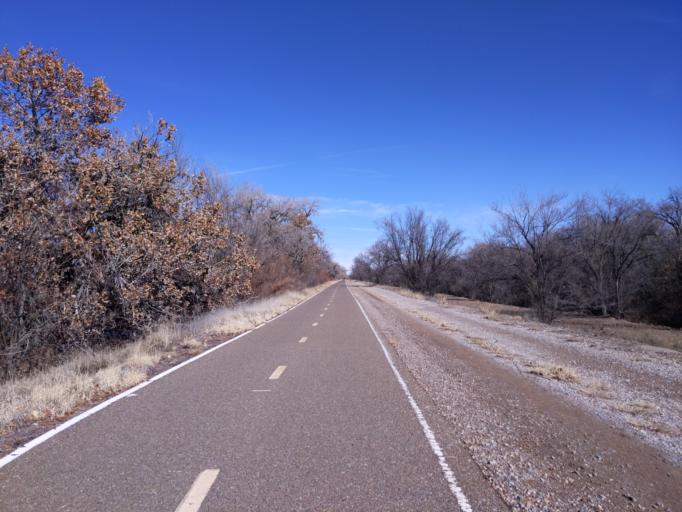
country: US
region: New Mexico
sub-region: Bernalillo County
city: Lee Acres
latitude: 35.1510
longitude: -106.6707
